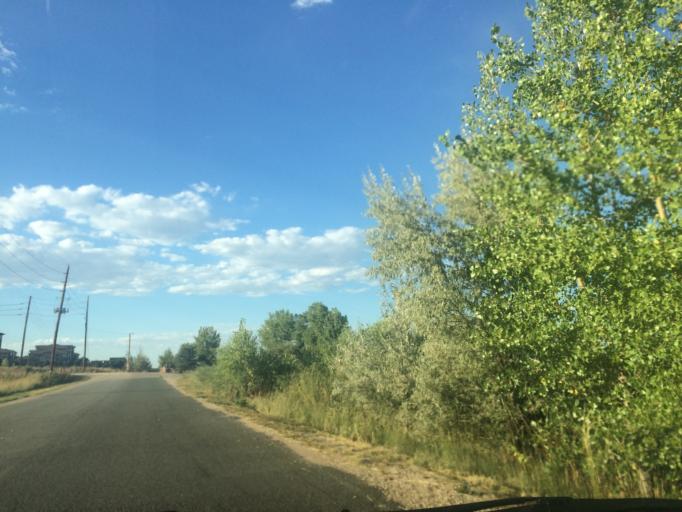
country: US
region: Colorado
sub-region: Boulder County
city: Louisville
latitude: 39.9421
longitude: -105.1187
